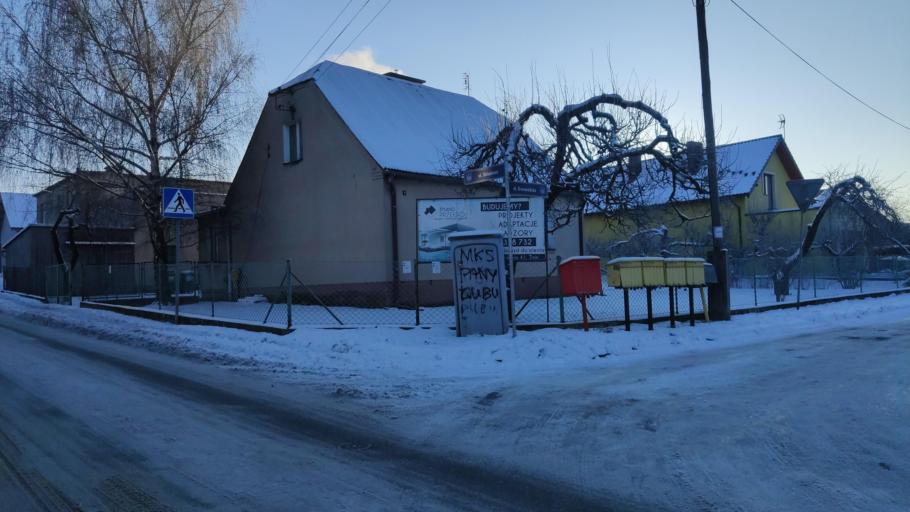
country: PL
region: Kujawsko-Pomorskie
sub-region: Powiat zninski
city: Znin
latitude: 52.8467
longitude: 17.7480
